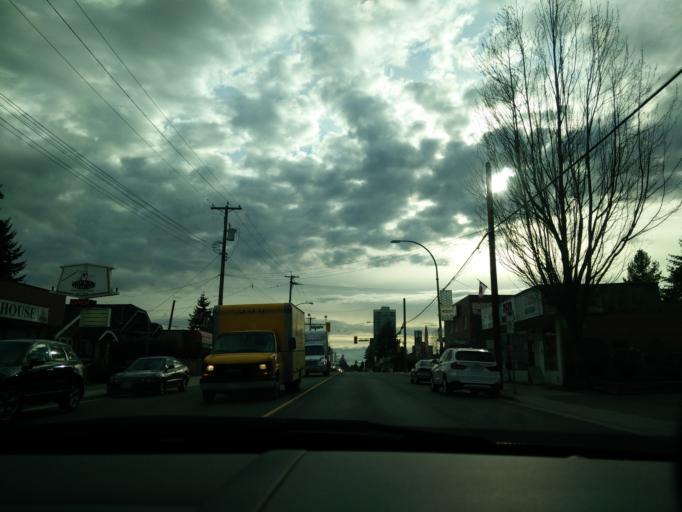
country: CA
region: British Columbia
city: New Westminster
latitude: 49.2225
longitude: -122.9440
